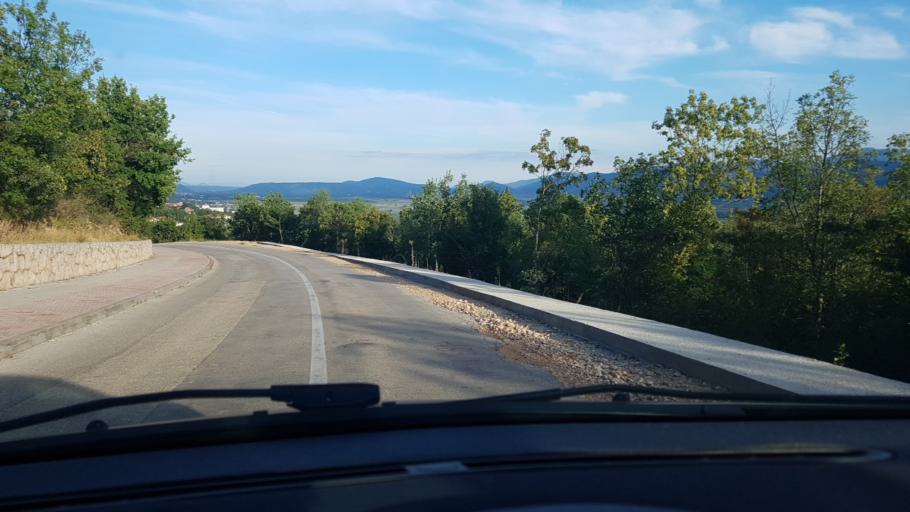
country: HR
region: Splitsko-Dalmatinska
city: Imotski
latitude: 43.4503
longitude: 17.1998
